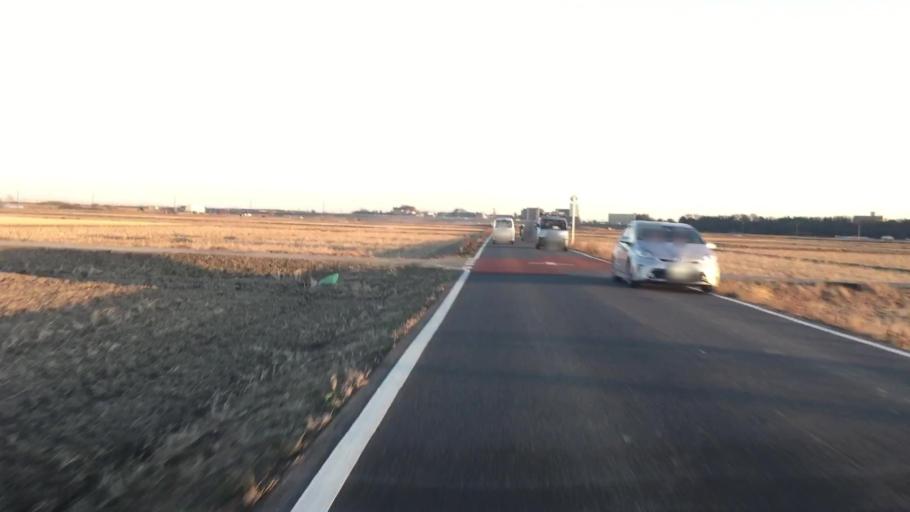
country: JP
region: Chiba
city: Abiko
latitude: 35.8905
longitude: 140.0300
